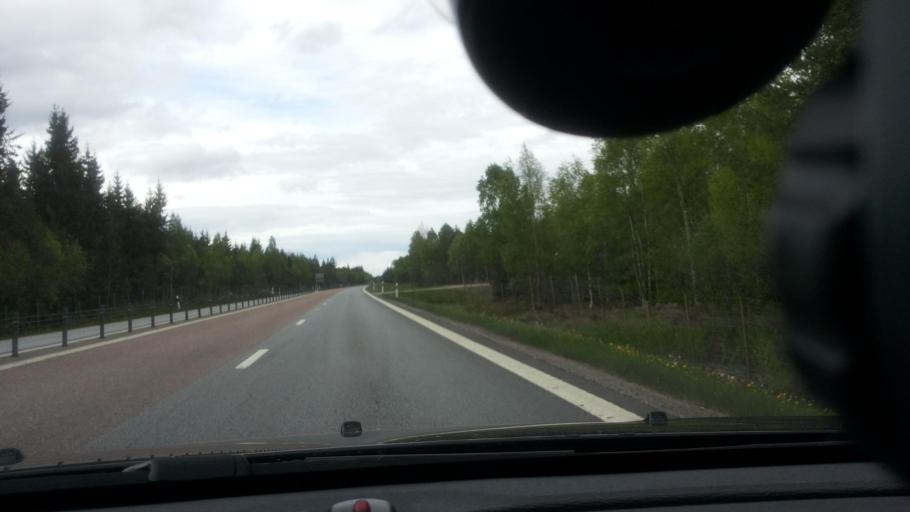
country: SE
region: Gaevleborg
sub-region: Gavle Kommun
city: Norrsundet
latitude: 60.9069
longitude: 17.0148
